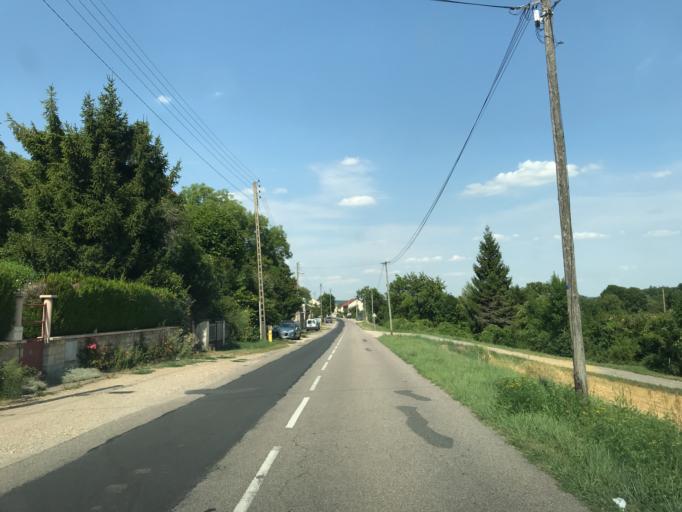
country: FR
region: Ile-de-France
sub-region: Departement des Yvelines
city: Freneuse
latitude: 49.0492
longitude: 1.5865
